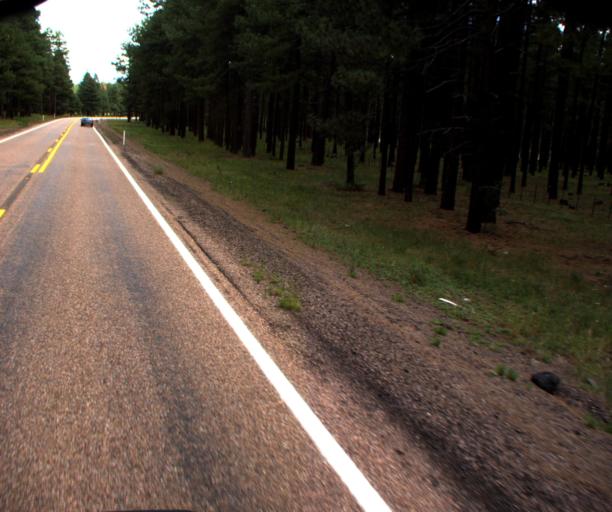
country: US
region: Arizona
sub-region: Navajo County
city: Pinetop-Lakeside
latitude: 34.0787
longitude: -109.7948
